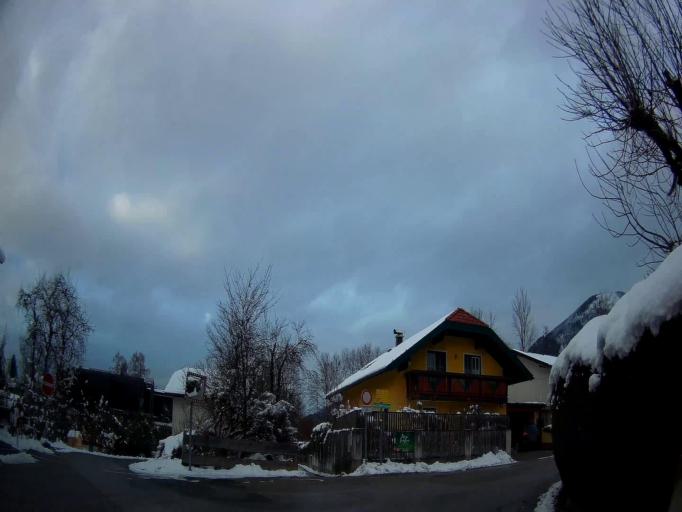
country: AT
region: Salzburg
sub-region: Politischer Bezirk Salzburg-Umgebung
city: Elsbethen
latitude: 47.7782
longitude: 13.0869
